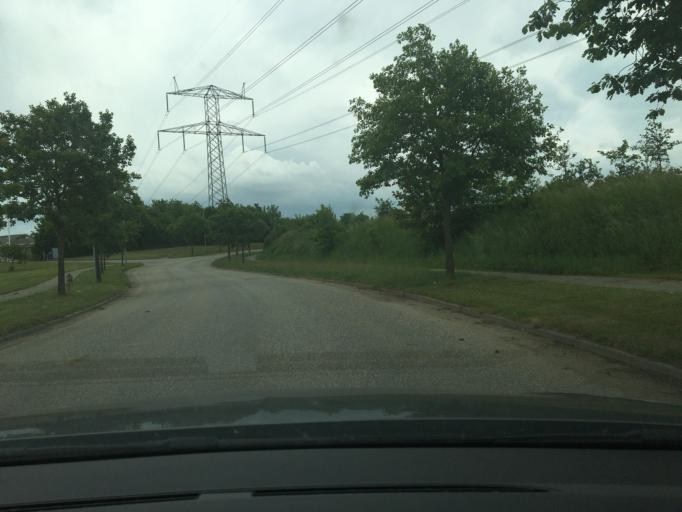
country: DK
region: South Denmark
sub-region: Kolding Kommune
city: Kolding
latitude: 55.5423
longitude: 9.5066
